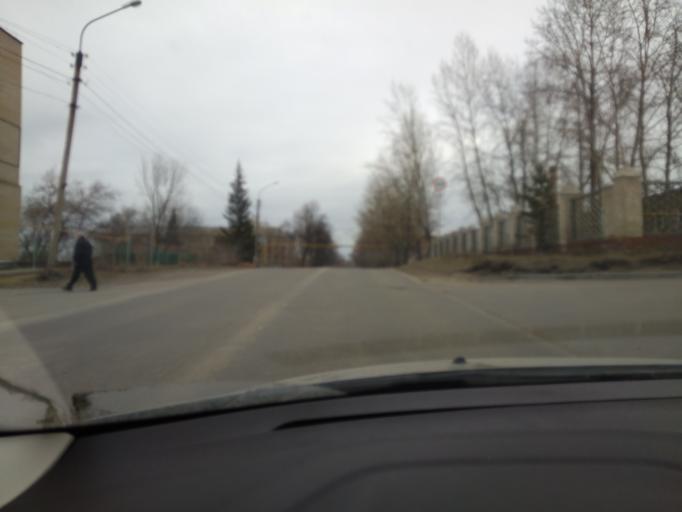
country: RU
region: Chelyabinsk
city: Kyshtym
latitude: 55.7047
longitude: 60.5224
